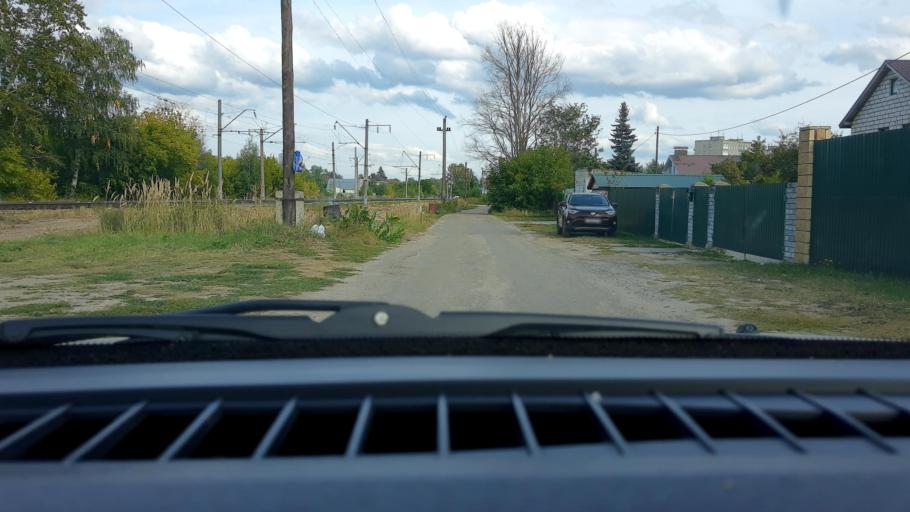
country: RU
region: Nizjnij Novgorod
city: Gorbatovka
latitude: 56.3721
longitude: 43.8182
